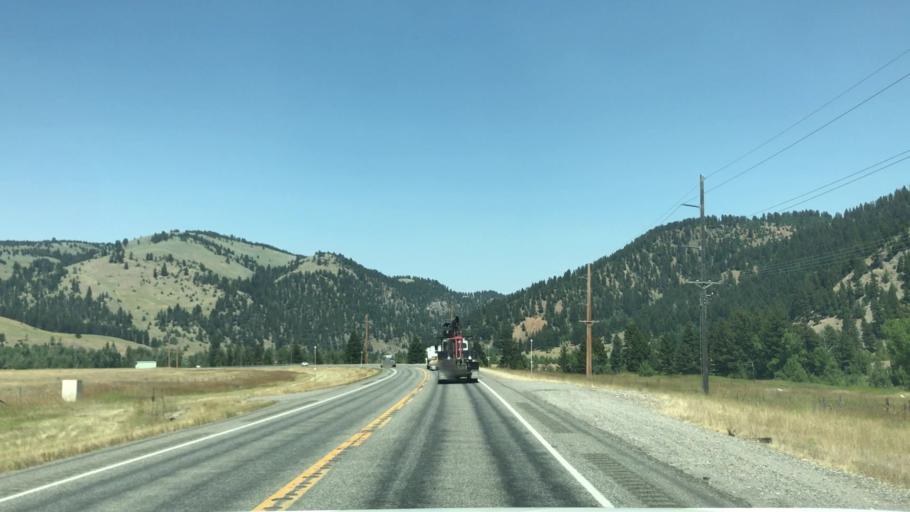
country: US
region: Montana
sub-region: Gallatin County
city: Four Corners
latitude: 45.4854
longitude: -111.2710
